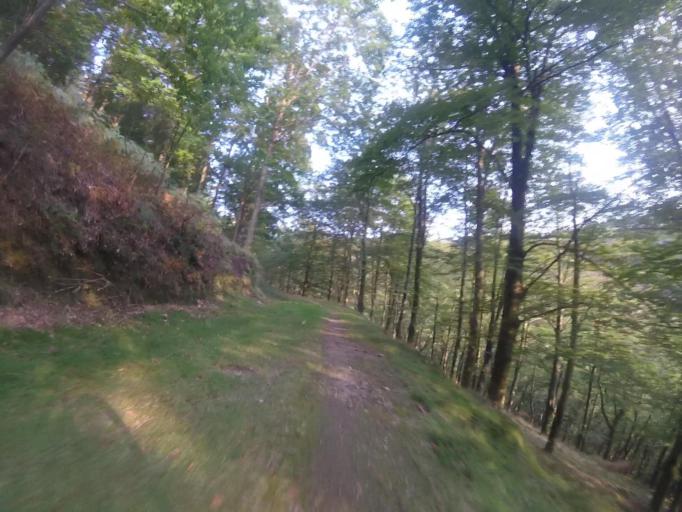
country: ES
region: Navarre
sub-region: Provincia de Navarra
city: Arano
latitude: 43.2526
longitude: -1.8322
